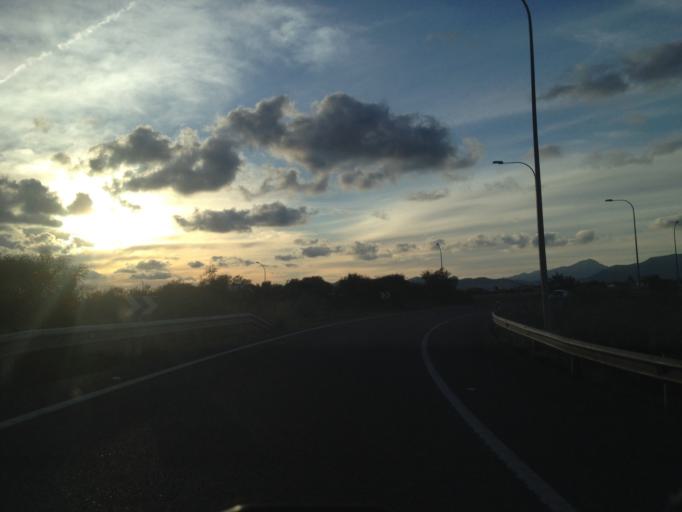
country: ES
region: Balearic Islands
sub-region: Illes Balears
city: Marratxi
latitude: 39.6138
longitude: 2.6974
